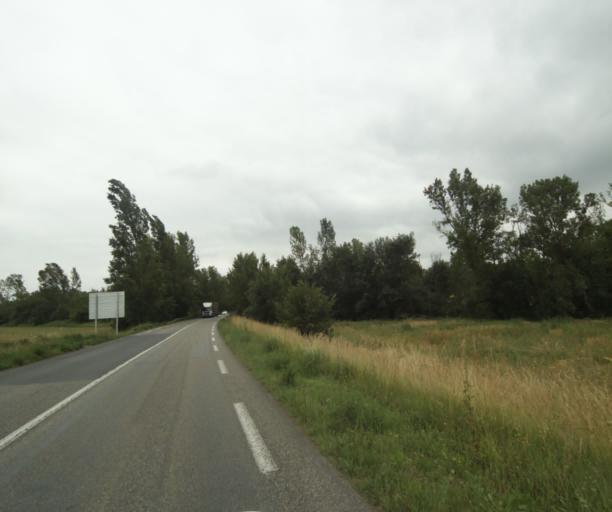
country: FR
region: Midi-Pyrenees
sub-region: Departement du Tarn-et-Garonne
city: Saint-Nauphary
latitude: 43.9885
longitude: 1.3932
